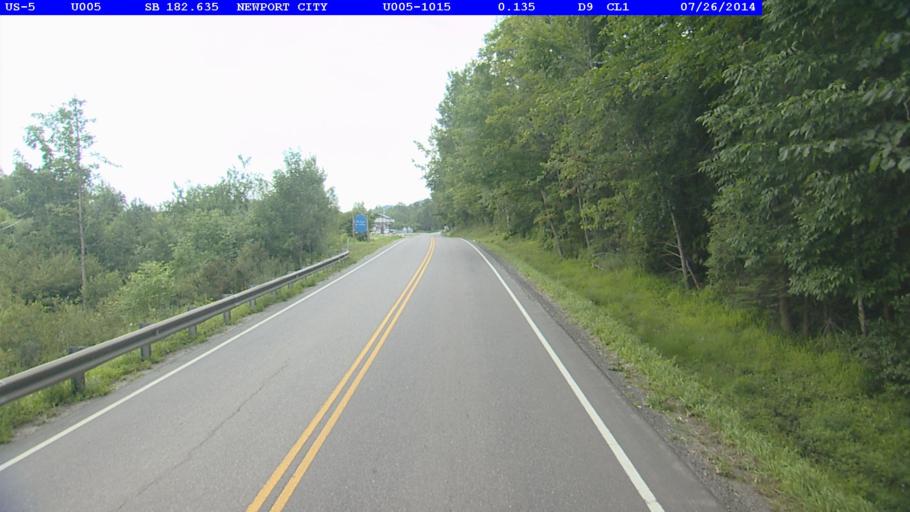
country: US
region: Vermont
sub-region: Orleans County
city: Newport
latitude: 44.9249
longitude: -72.2283
